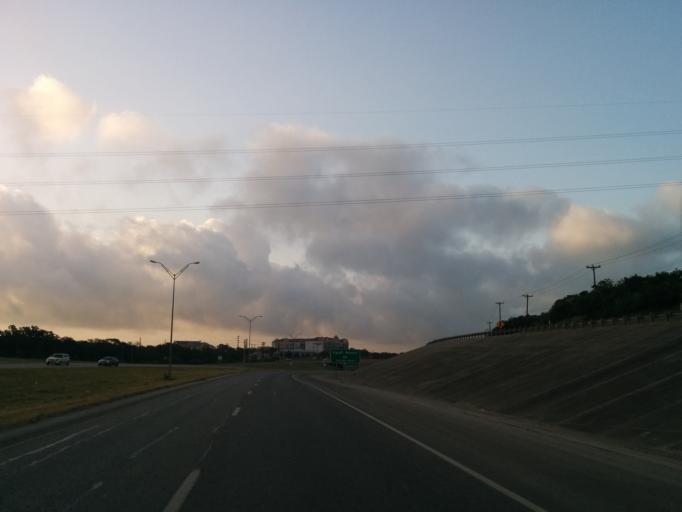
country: US
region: Texas
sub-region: Bexar County
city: Leon Valley
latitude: 29.4780
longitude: -98.7016
